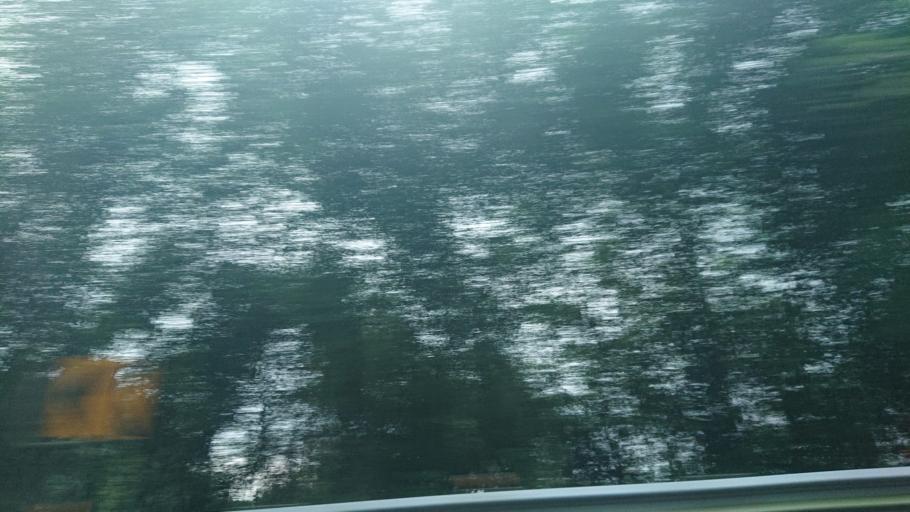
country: TW
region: Taiwan
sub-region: Chiayi
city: Jiayi Shi
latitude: 23.4613
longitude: 120.7220
